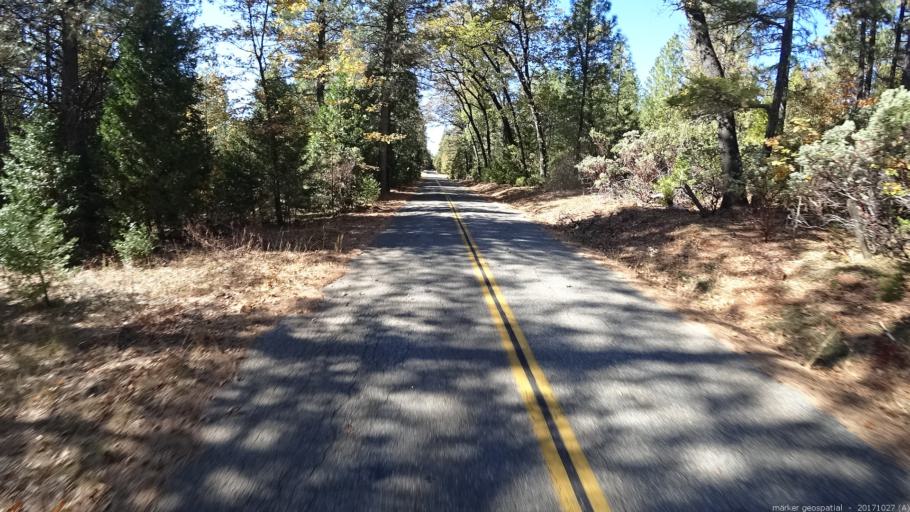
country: US
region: California
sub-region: Shasta County
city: Bella Vista
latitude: 40.7179
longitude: -121.9980
